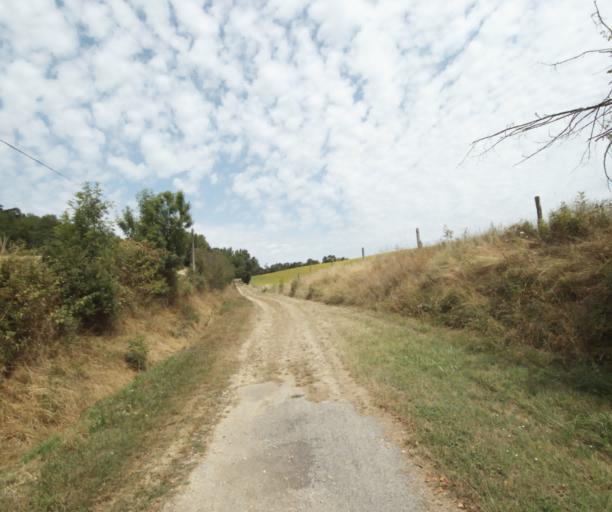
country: FR
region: Midi-Pyrenees
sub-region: Departement de la Haute-Garonne
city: Saint-Felix-Lauragais
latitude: 43.4466
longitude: 1.8920
